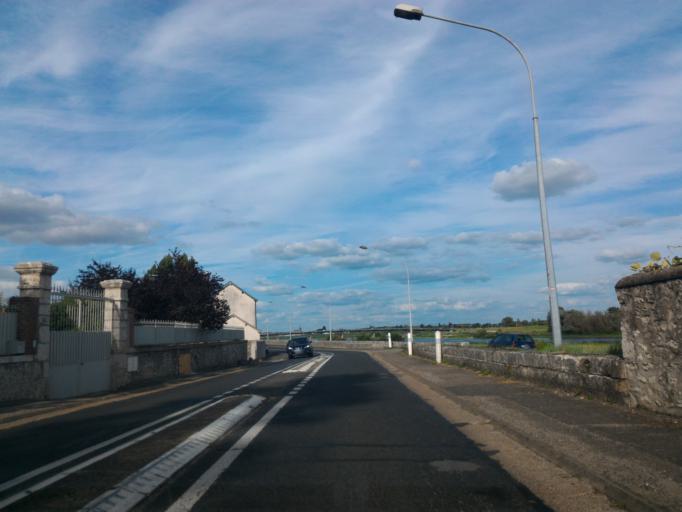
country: FR
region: Centre
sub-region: Departement du Loir-et-Cher
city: Blois
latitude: 47.5731
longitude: 1.3123
